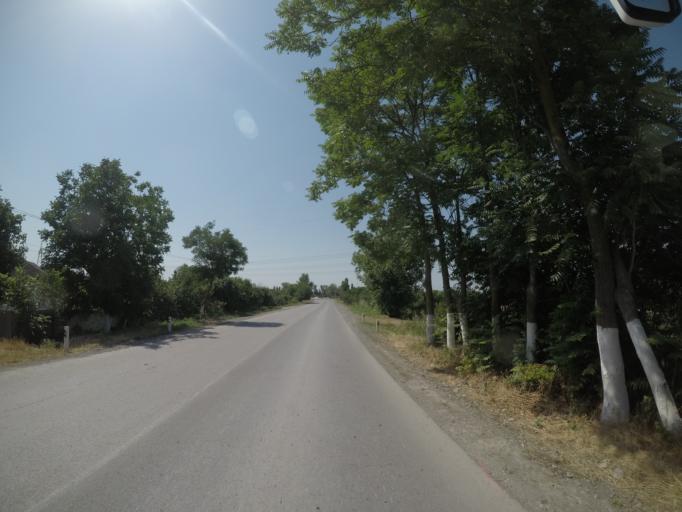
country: AZ
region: Agdas
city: Agdas
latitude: 40.7022
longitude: 47.5413
